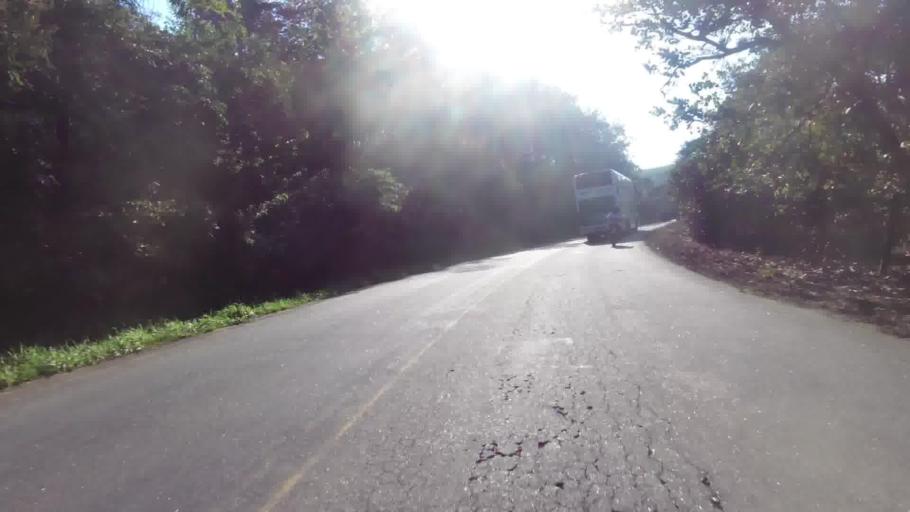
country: BR
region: Espirito Santo
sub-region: Alfredo Chaves
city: Alfredo Chaves
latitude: -20.6739
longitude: -40.7090
